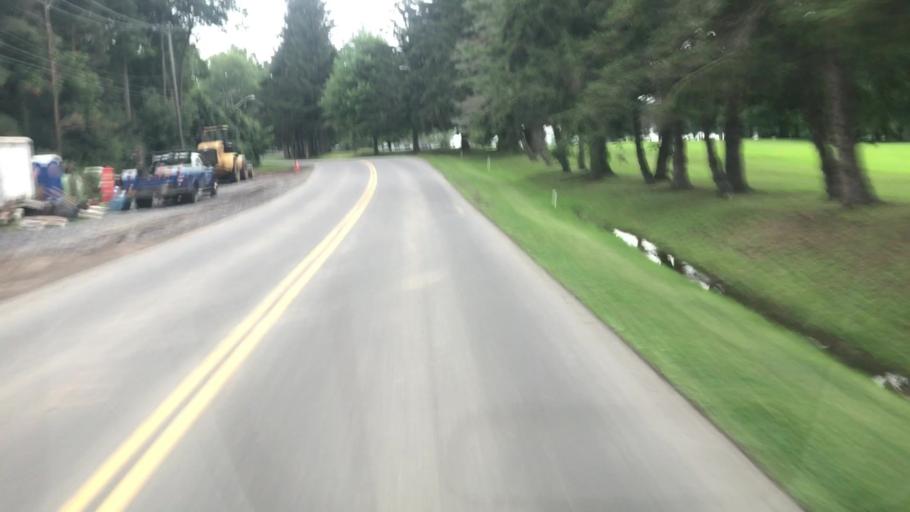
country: US
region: New York
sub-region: Cayuga County
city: Melrose Park
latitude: 42.9056
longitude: -76.5292
